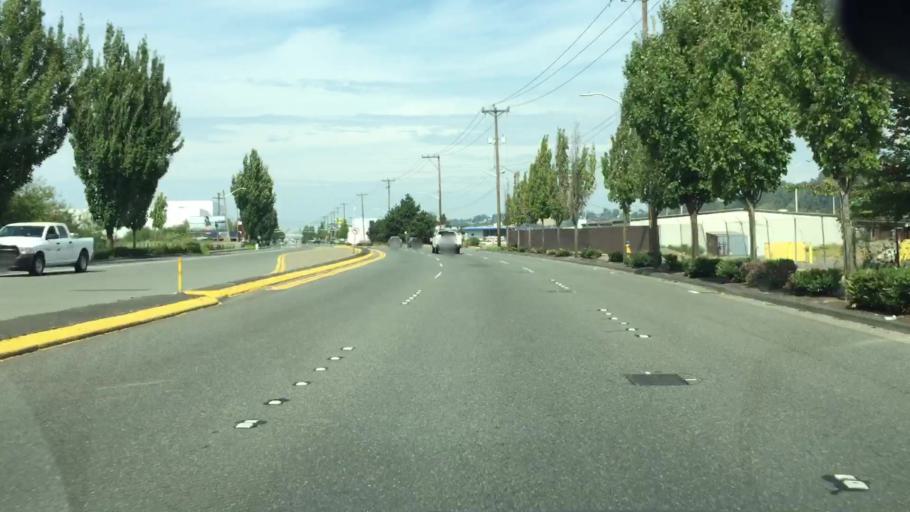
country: US
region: Washington
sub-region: King County
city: Riverton
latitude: 47.5083
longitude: -122.2913
